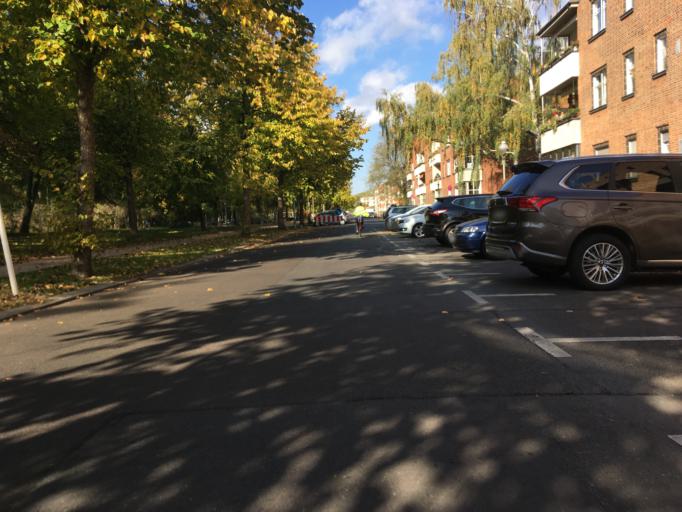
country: DE
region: Berlin
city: Wedding Bezirk
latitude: 52.5589
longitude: 13.3502
